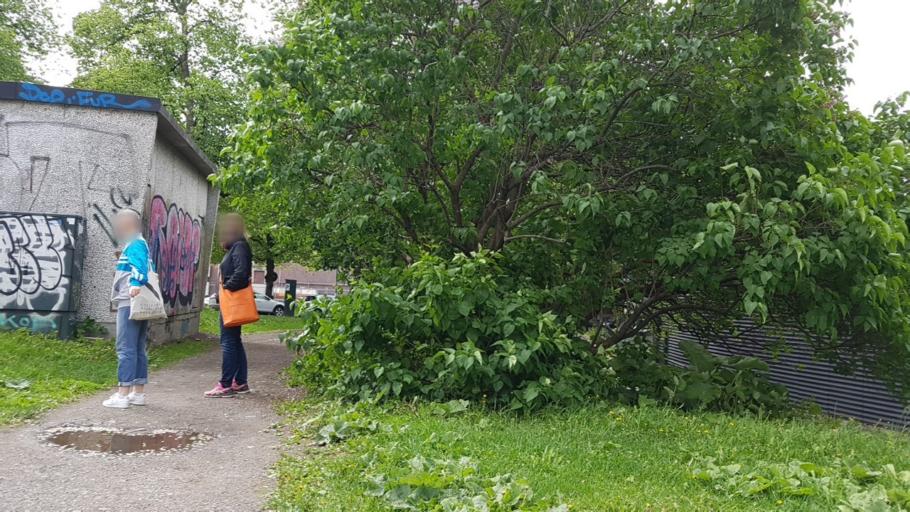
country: NO
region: Oslo
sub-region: Oslo
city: Oslo
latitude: 59.9270
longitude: 10.7661
